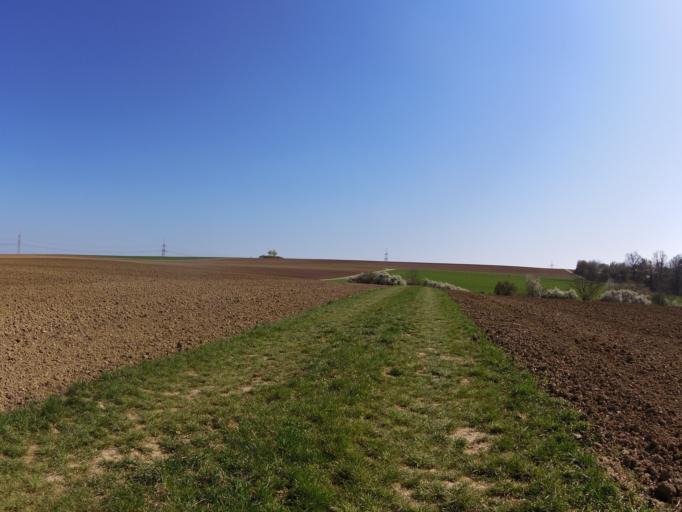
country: DE
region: Bavaria
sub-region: Regierungsbezirk Unterfranken
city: Rottendorf
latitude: 49.8192
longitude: 10.0695
